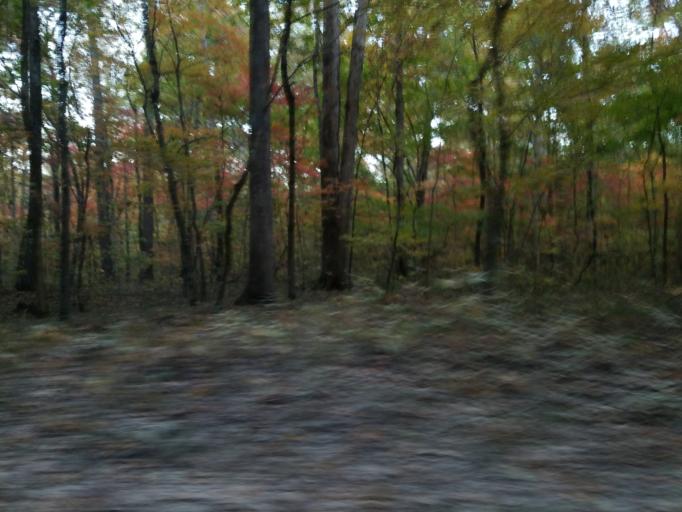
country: US
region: Georgia
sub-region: Gordon County
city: Calhoun
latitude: 34.6131
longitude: -85.0468
